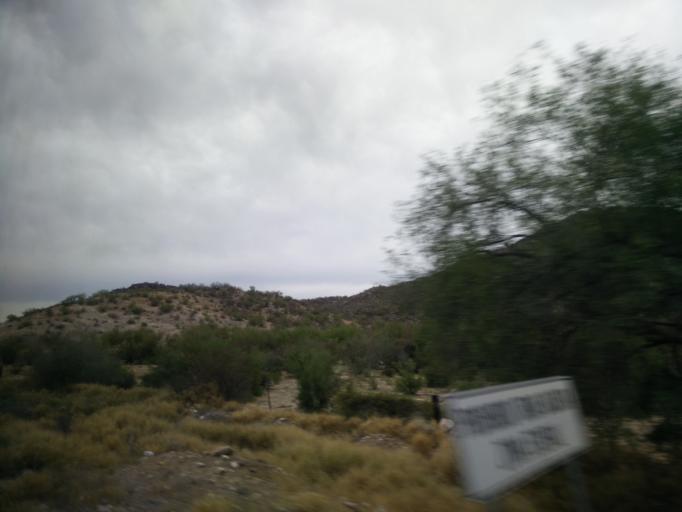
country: MX
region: Sonora
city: Hermosillo
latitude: 28.9766
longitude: -110.9641
